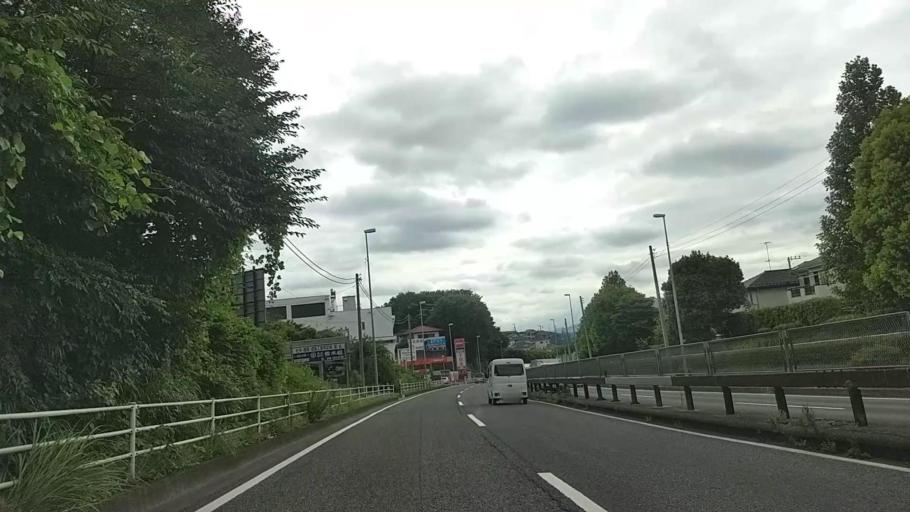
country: JP
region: Kanagawa
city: Zama
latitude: 35.4655
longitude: 139.4055
